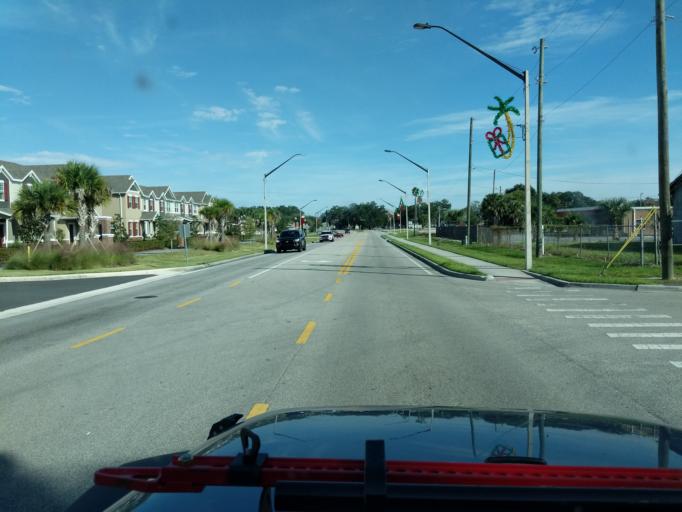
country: US
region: Florida
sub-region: Orange County
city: Winter Garden
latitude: 28.5668
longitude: -81.5784
